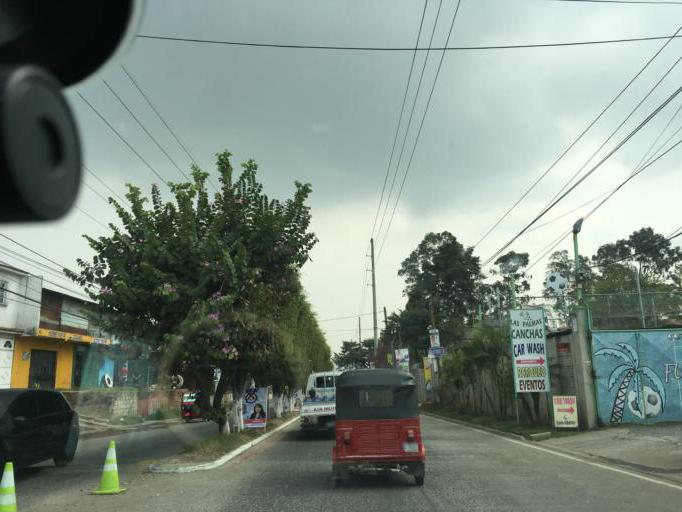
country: GT
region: Guatemala
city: Petapa
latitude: 14.5050
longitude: -90.5600
